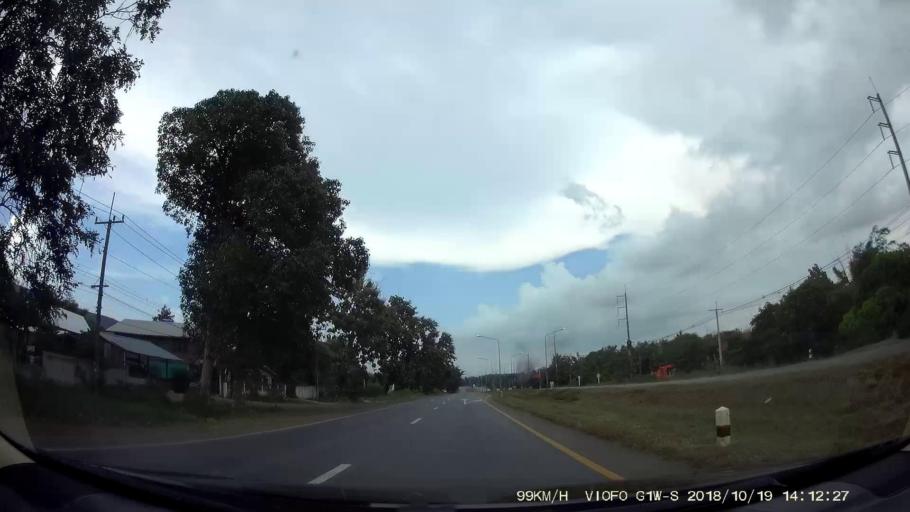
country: TH
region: Chaiyaphum
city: Khon Sawan
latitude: 15.9480
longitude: 102.1735
